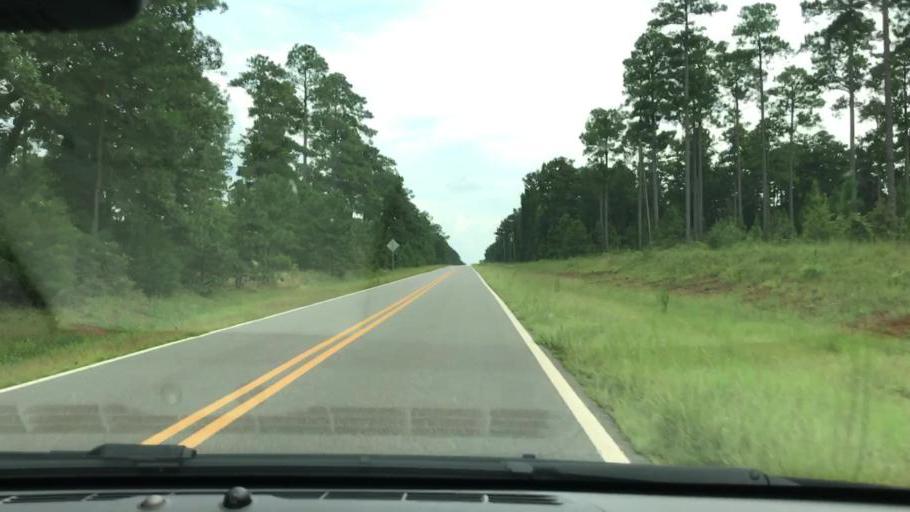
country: US
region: Georgia
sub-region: Early County
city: Blakely
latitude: 31.4604
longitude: -84.9197
